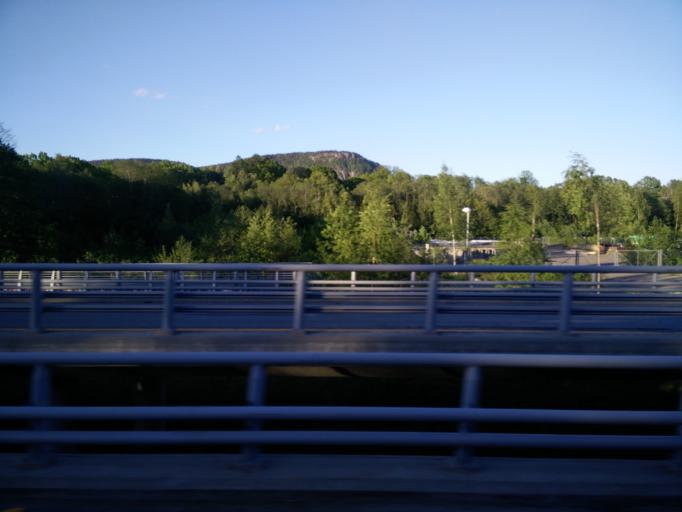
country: NO
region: Akershus
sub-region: Baerum
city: Skui
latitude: 59.9107
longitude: 10.4776
